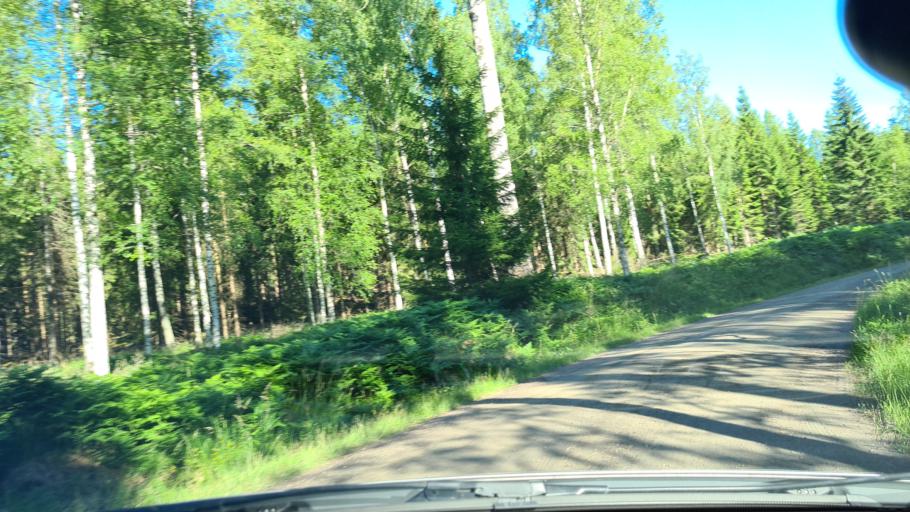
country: SE
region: Soedermanland
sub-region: Nykopings Kommun
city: Stigtomta
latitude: 58.9275
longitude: 16.8990
